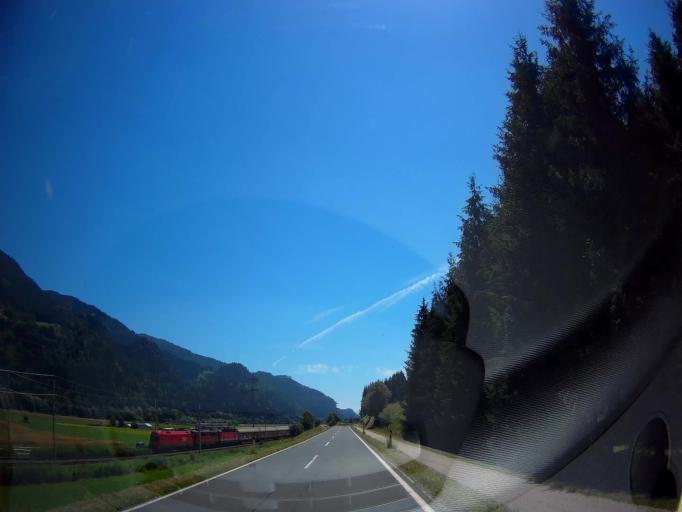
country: AT
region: Carinthia
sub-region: Politischer Bezirk Sankt Veit an der Glan
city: Micheldorf
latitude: 46.9304
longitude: 14.4262
